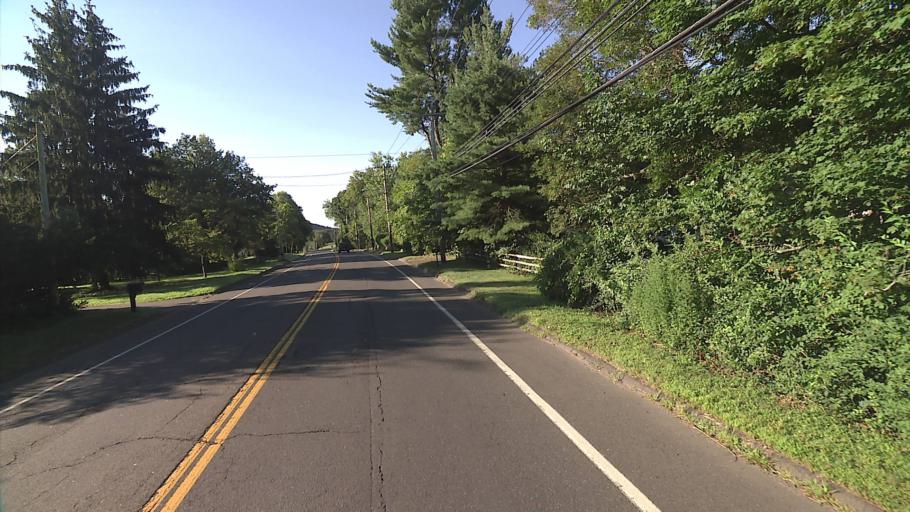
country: US
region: Connecticut
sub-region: New Haven County
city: Hamden
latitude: 41.4396
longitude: -72.9103
